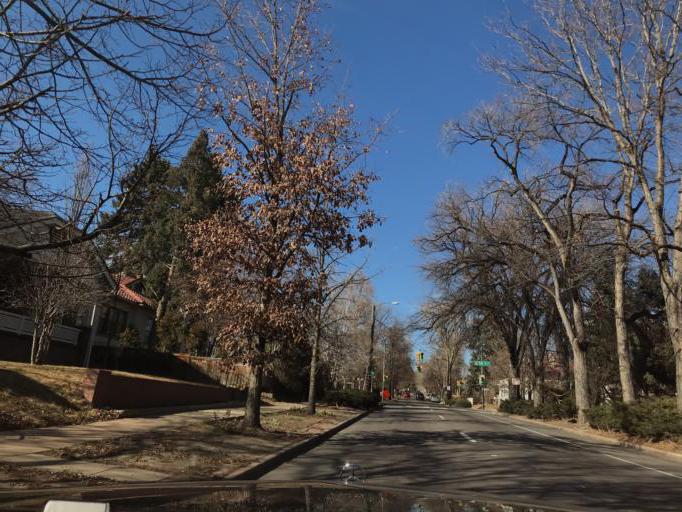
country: US
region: Colorado
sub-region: Denver County
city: Denver
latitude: 39.7265
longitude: -104.9591
